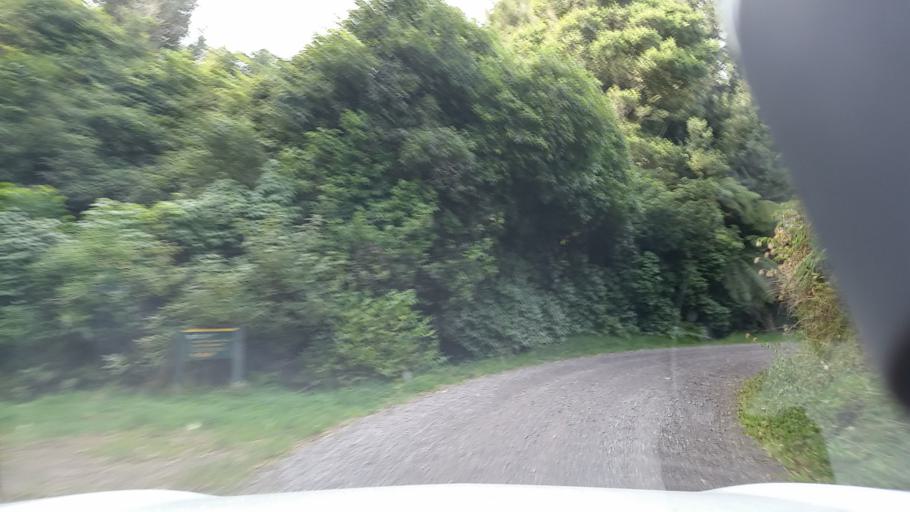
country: NZ
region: Bay of Plenty
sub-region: Rotorua District
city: Rotorua
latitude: -37.9643
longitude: 176.3082
